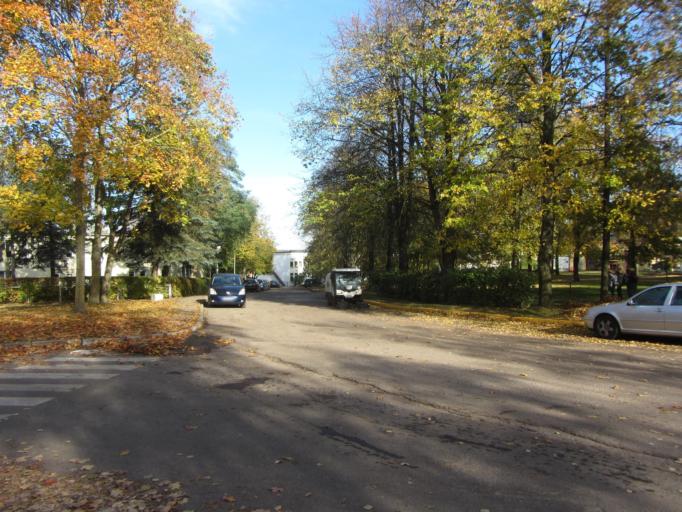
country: LT
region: Vilnius County
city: Elektrenai
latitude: 54.7874
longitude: 24.6651
